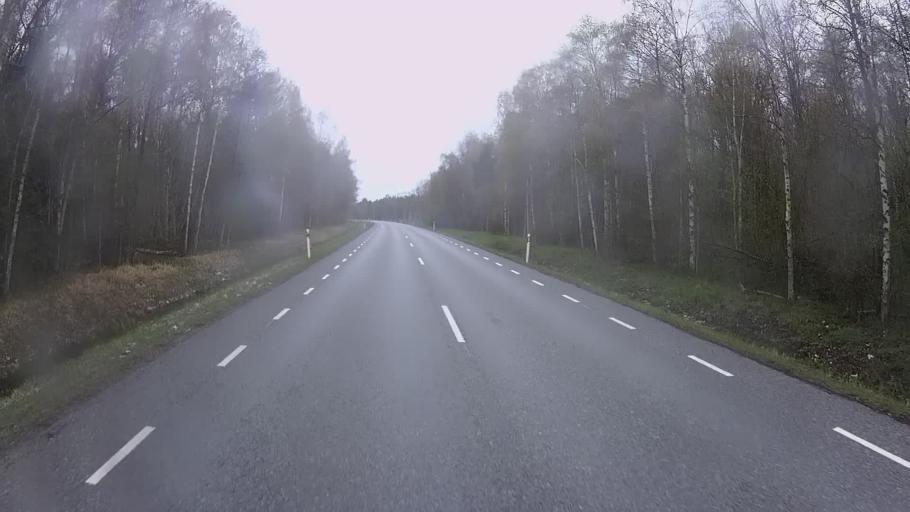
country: EE
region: Hiiumaa
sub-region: Kaerdla linn
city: Kardla
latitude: 59.0041
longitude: 22.5612
